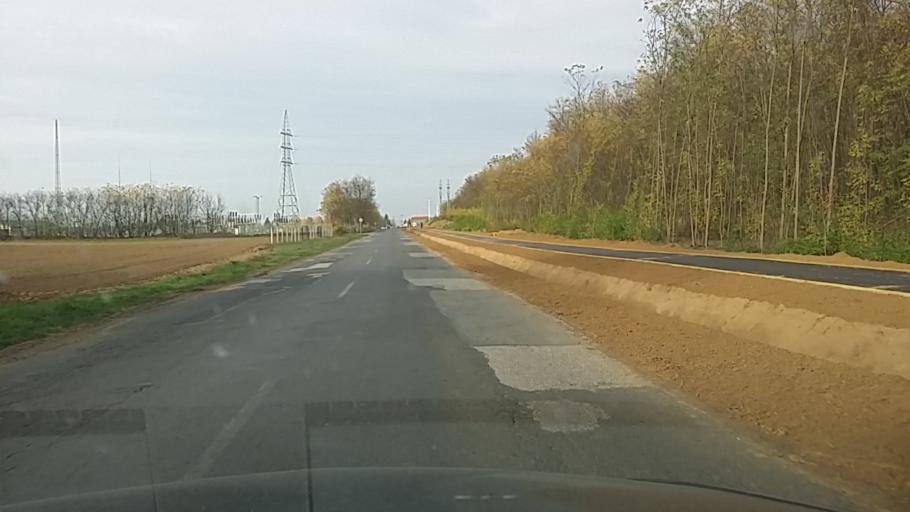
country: HU
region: Szabolcs-Szatmar-Bereg
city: Nyirbogdany
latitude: 48.0711
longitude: 21.8601
